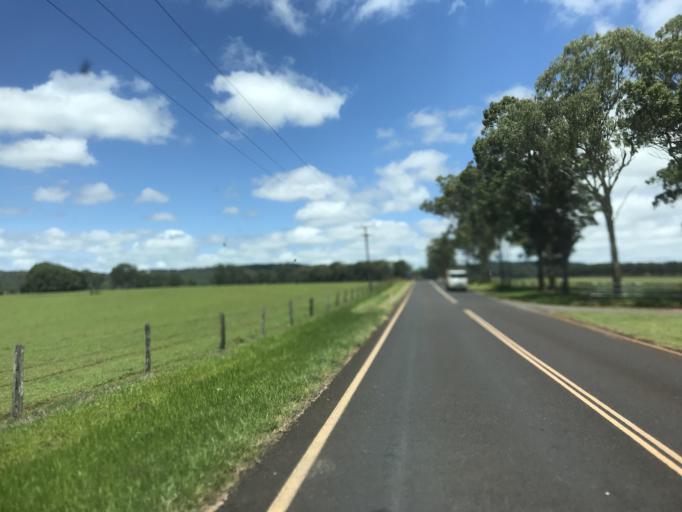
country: AU
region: Queensland
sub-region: Tablelands
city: Ravenshoe
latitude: -17.5127
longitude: 145.4512
